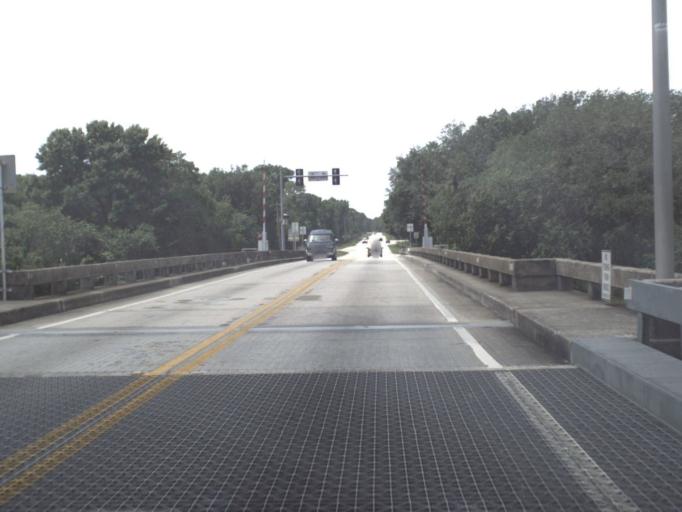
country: US
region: Florida
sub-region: Lake County
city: Lake Mack-Forest Hills
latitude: 29.0087
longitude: -81.3821
